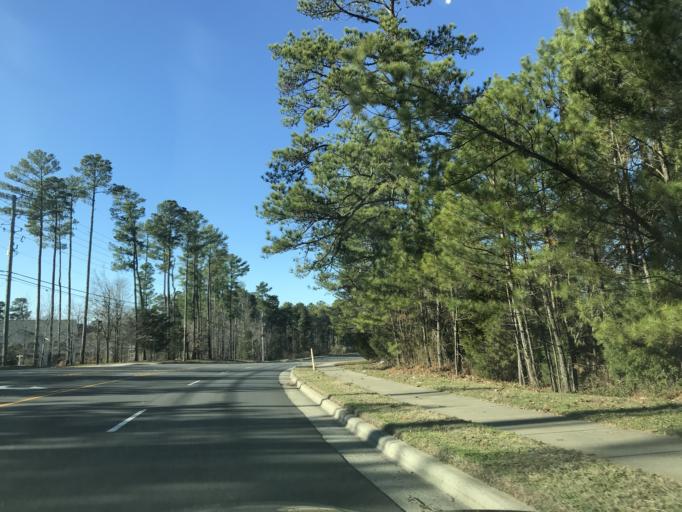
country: US
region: North Carolina
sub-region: Wake County
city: Morrisville
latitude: 35.8982
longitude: -78.8065
